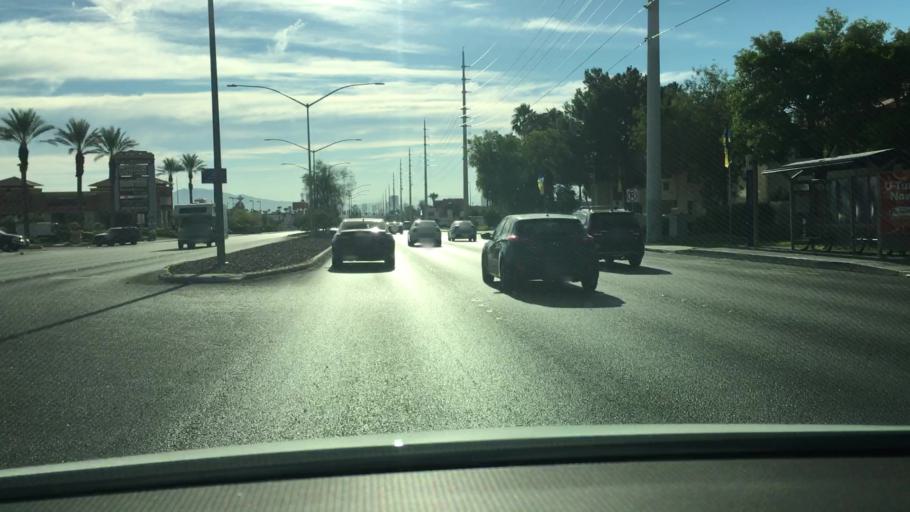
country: US
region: Nevada
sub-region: Clark County
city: Spring Valley
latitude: 36.1440
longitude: -115.2743
